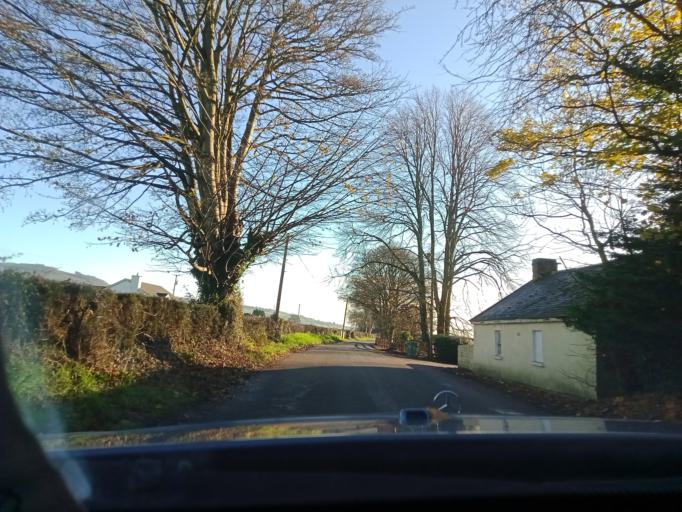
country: IE
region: Leinster
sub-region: Kilkenny
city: Piltown
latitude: 52.3647
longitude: -7.3199
